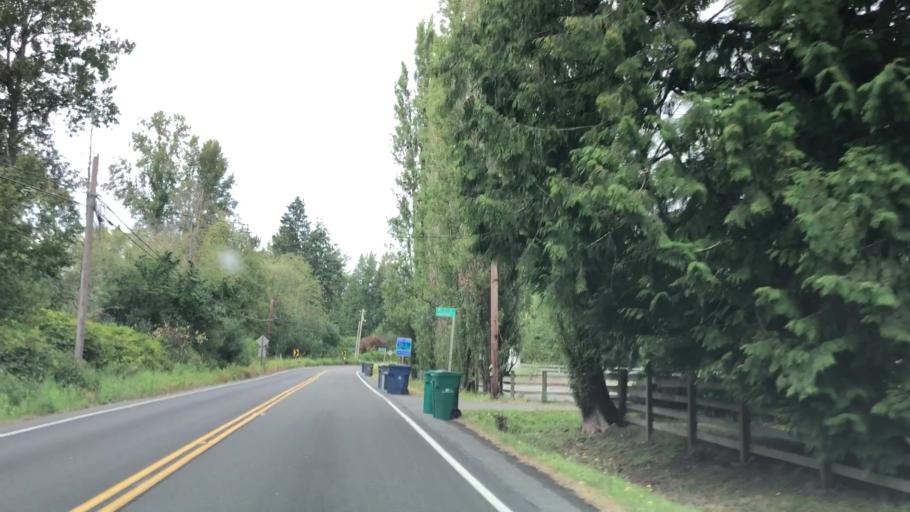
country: US
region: Washington
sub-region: King County
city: Cottage Lake
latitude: 47.7370
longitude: -122.0745
